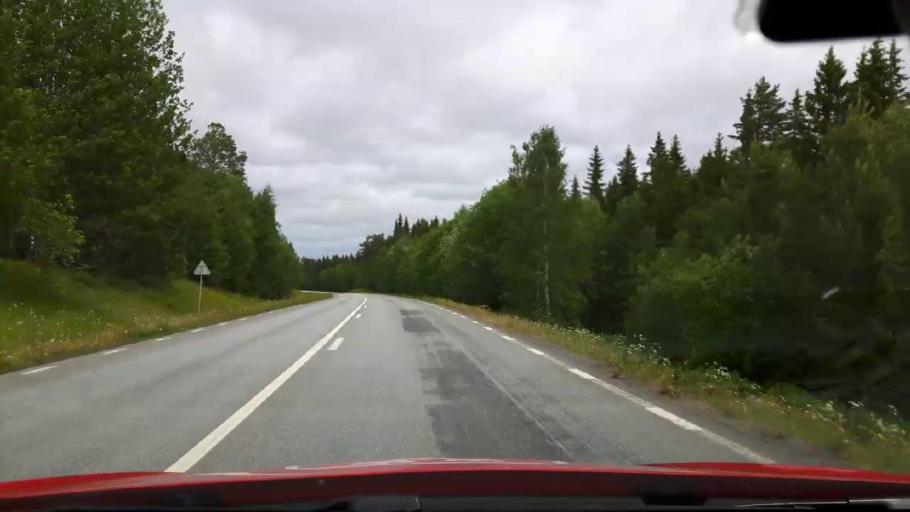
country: SE
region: Jaemtland
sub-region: Krokoms Kommun
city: Krokom
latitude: 63.3642
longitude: 14.5058
